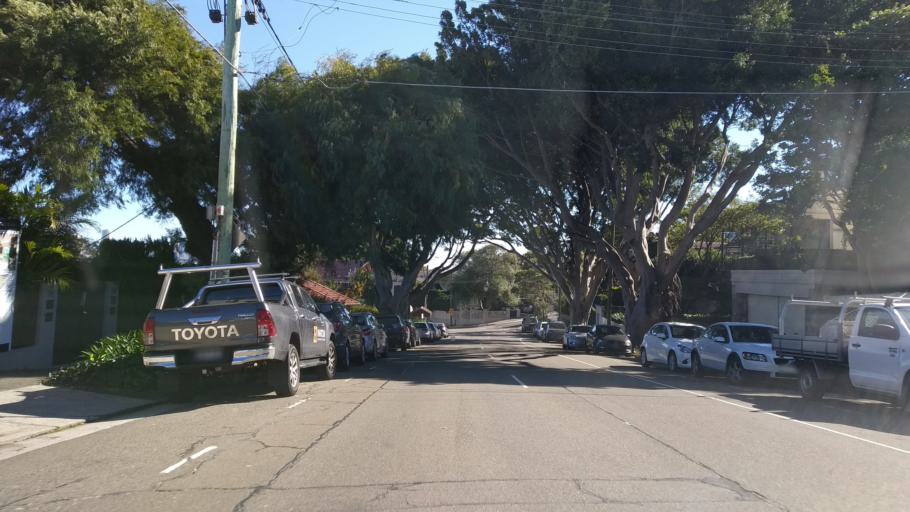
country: AU
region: New South Wales
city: Edgecliff
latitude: -33.8829
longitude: 151.2530
